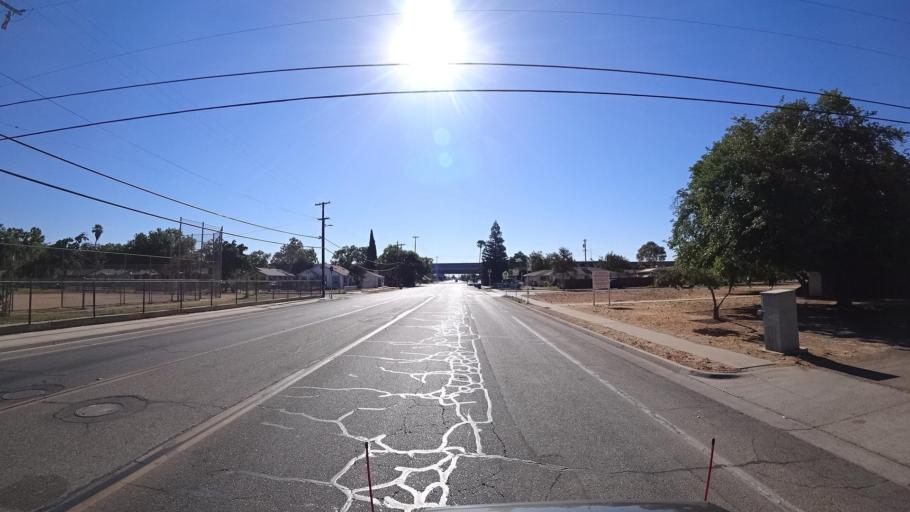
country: US
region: California
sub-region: Fresno County
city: Fresno
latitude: 36.7141
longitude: -119.7869
